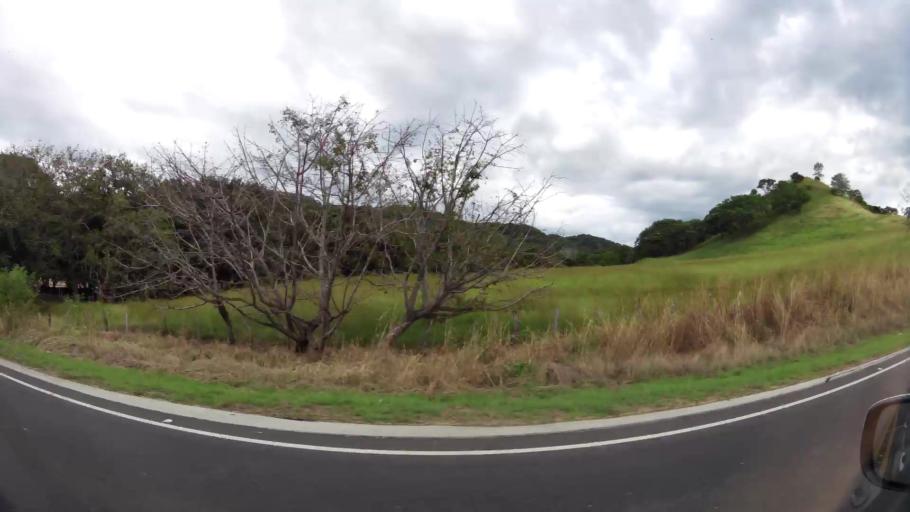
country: CR
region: Guanacaste
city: Nandayure
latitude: 10.2383
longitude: -85.2204
